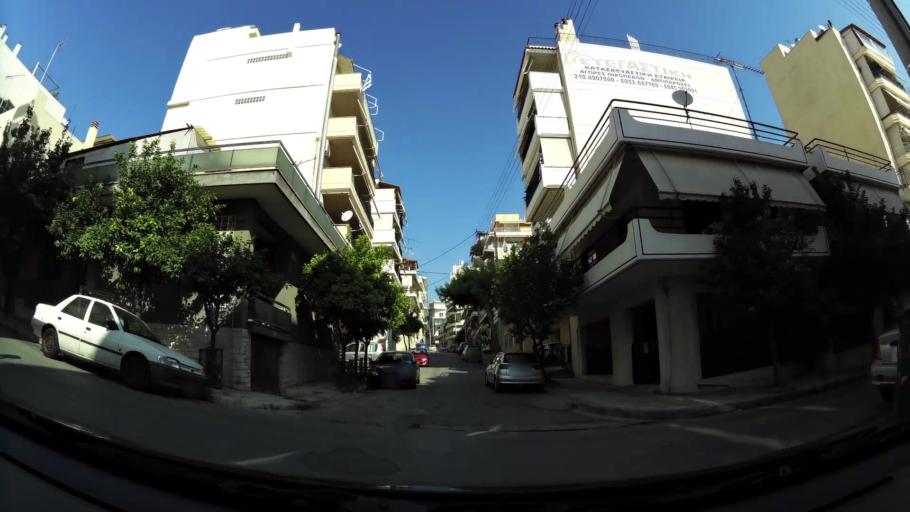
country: GR
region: Attica
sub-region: Nomos Piraios
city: Drapetsona
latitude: 37.9530
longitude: 23.6202
